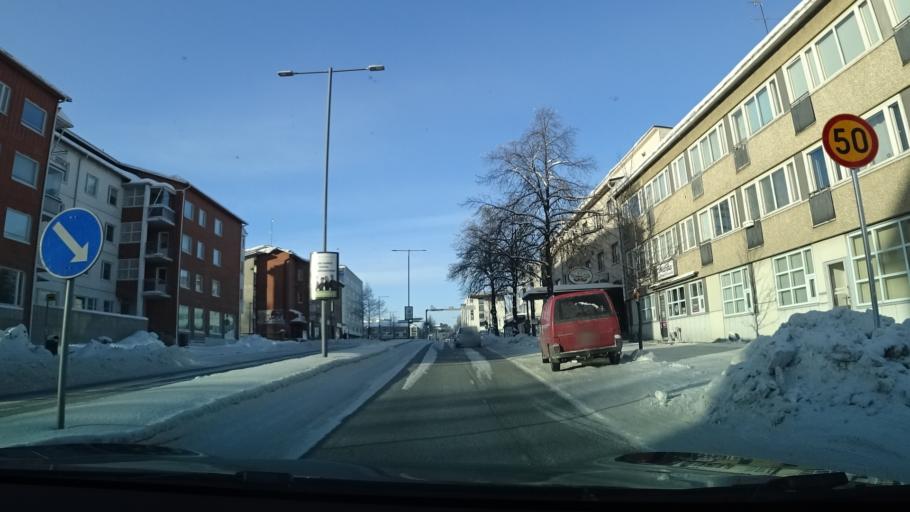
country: FI
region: South Karelia
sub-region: Lappeenranta
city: Lappeenranta
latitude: 61.0535
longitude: 28.1915
